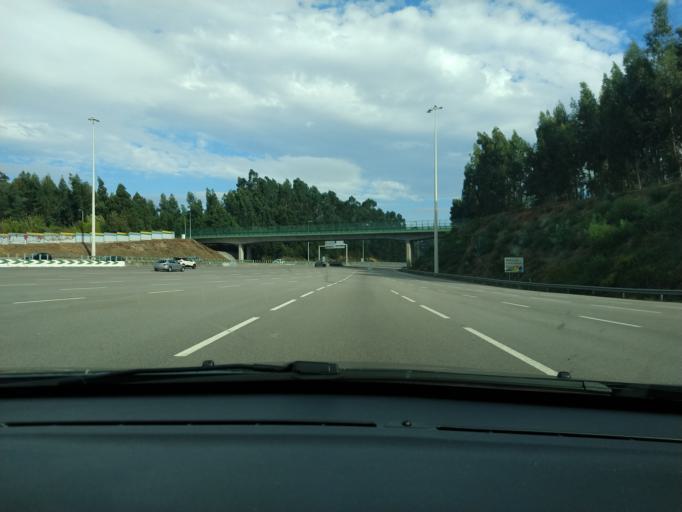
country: PT
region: Porto
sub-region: Vila Nova de Gaia
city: Grijo
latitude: 41.0180
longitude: -8.5809
